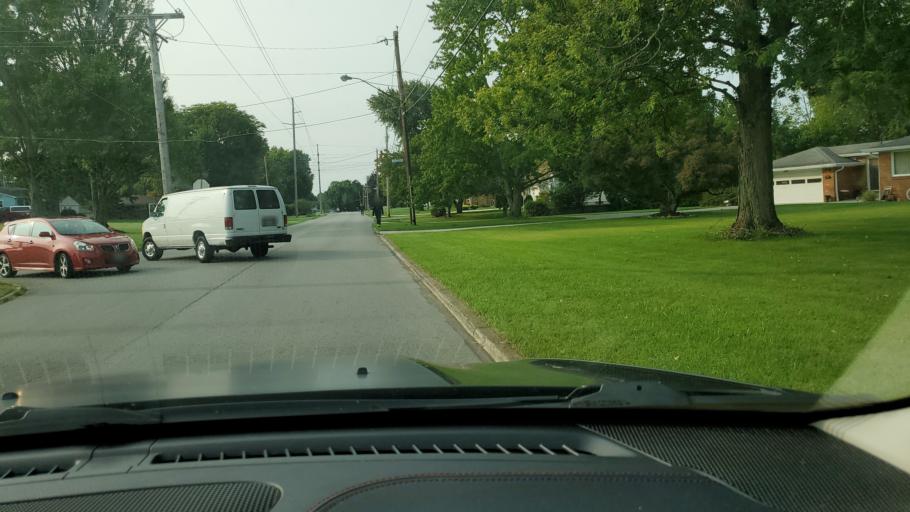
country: US
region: Ohio
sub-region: Mahoning County
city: Poland
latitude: 41.0337
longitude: -80.6212
